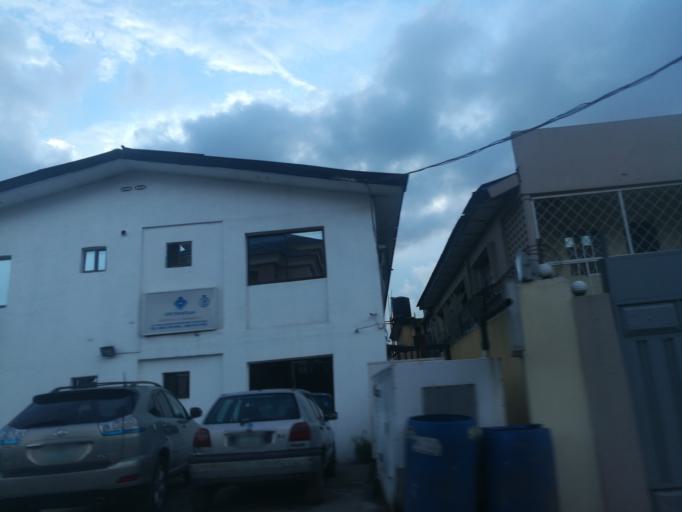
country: NG
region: Lagos
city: Somolu
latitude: 6.5624
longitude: 3.3707
